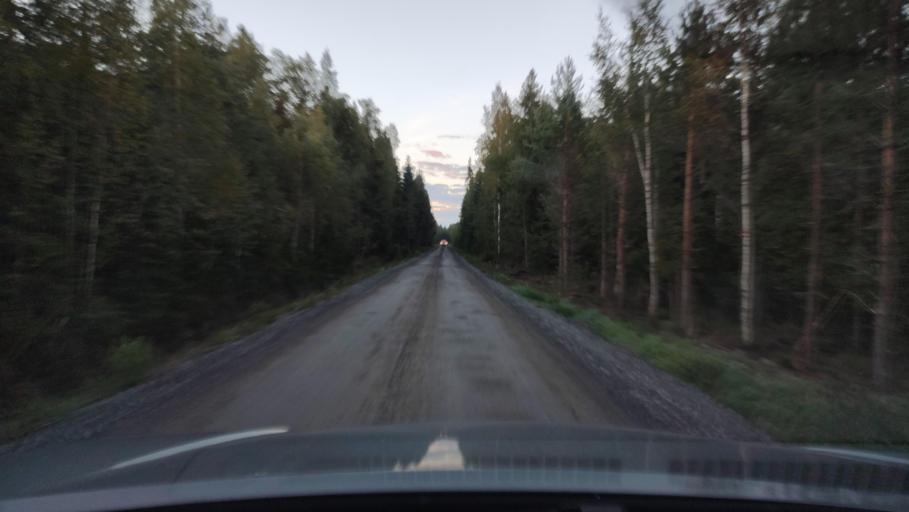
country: FI
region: Southern Ostrobothnia
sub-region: Suupohja
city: Karijoki
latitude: 62.1970
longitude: 21.5749
